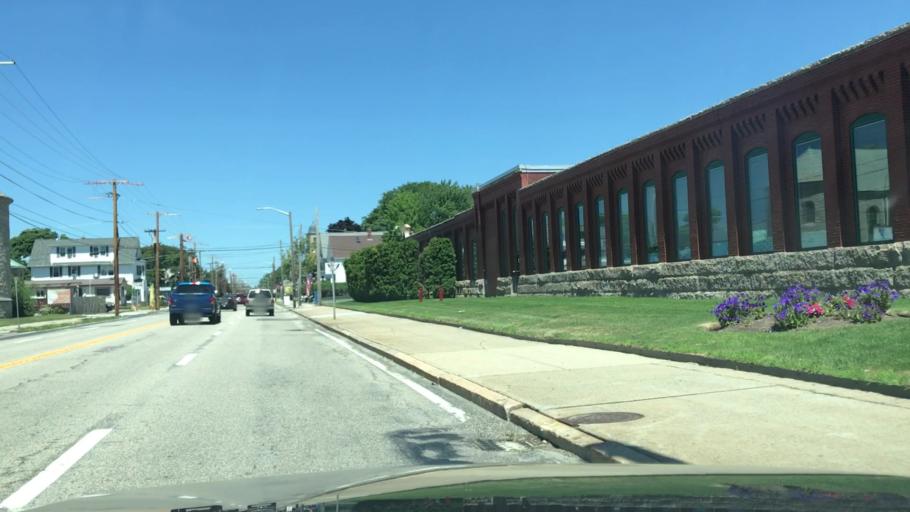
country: US
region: Massachusetts
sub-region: Bristol County
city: North Seekonk
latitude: 41.8835
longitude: -71.3541
